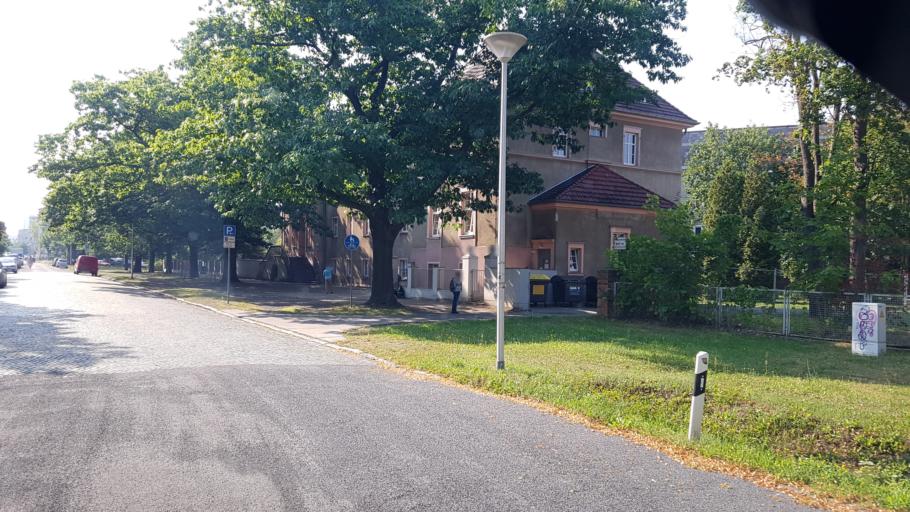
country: DE
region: Brandenburg
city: Cottbus
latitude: 51.7656
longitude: 14.3211
